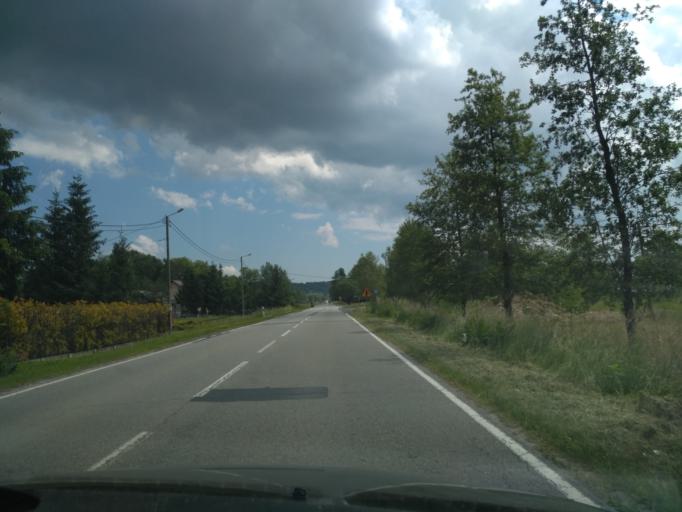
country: PL
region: Subcarpathian Voivodeship
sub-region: Powiat rzeszowski
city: Chmielnik
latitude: 49.9266
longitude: 22.1313
